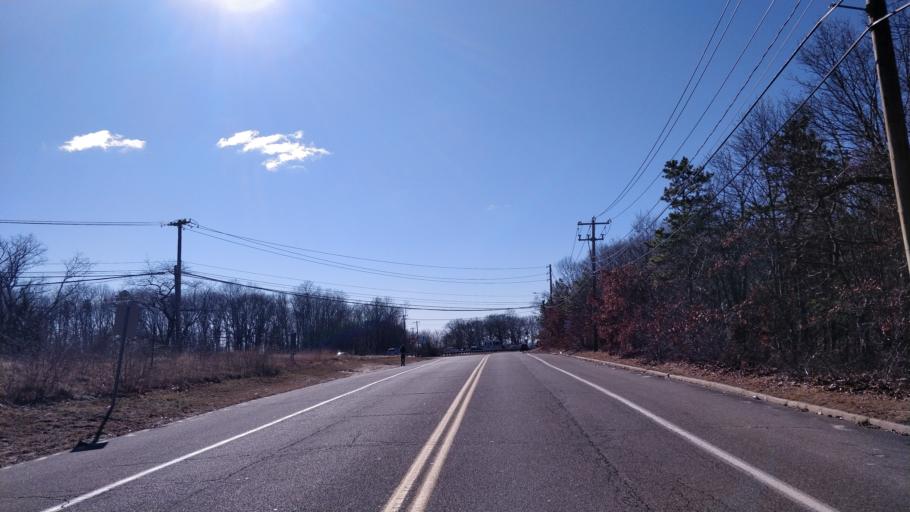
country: US
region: New York
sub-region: Suffolk County
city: Centereach
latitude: 40.8877
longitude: -73.1006
